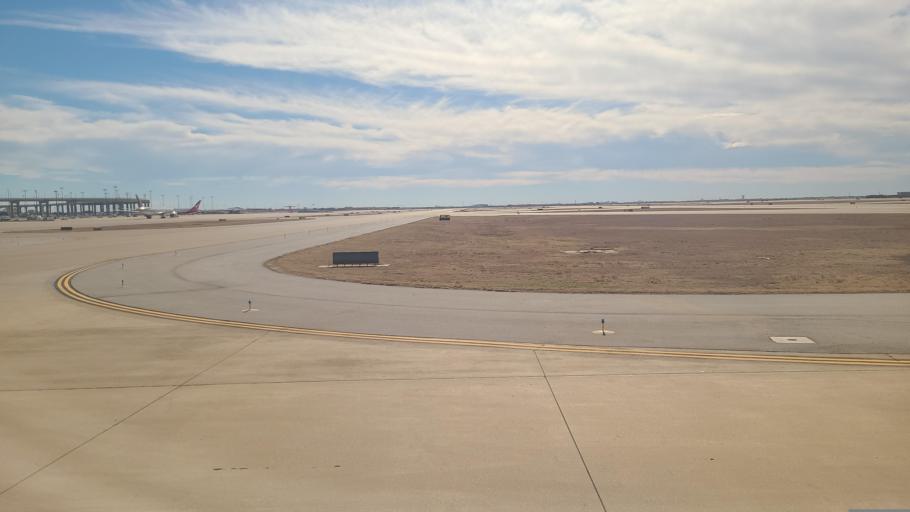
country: US
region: Texas
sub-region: Tarrant County
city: Grapevine
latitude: 32.8976
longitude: -97.0494
